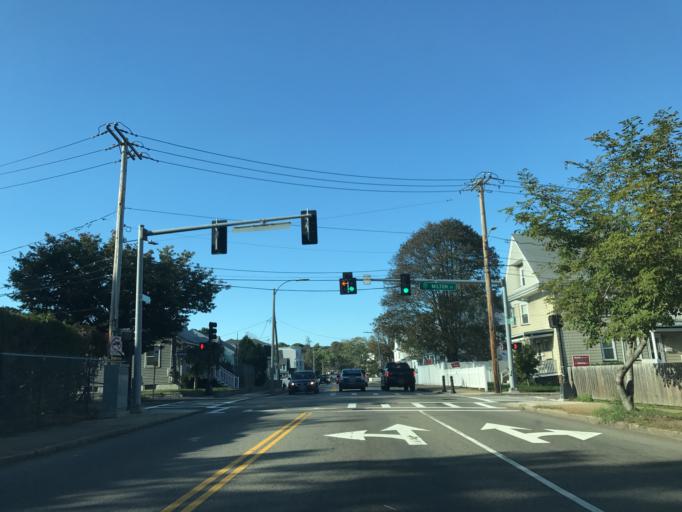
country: US
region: Massachusetts
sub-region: Norfolk County
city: Milton
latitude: 42.2801
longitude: -71.0545
